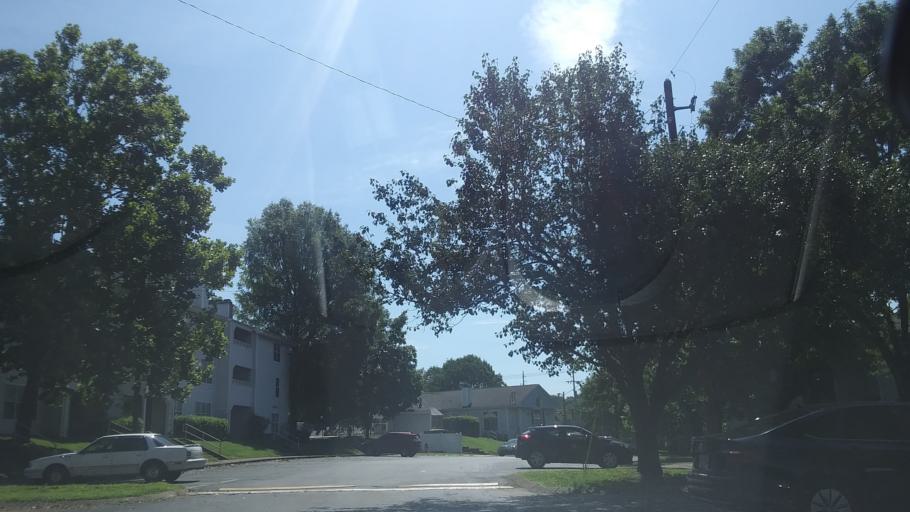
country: US
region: Tennessee
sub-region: Rutherford County
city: La Vergne
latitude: 36.0741
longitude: -86.6650
